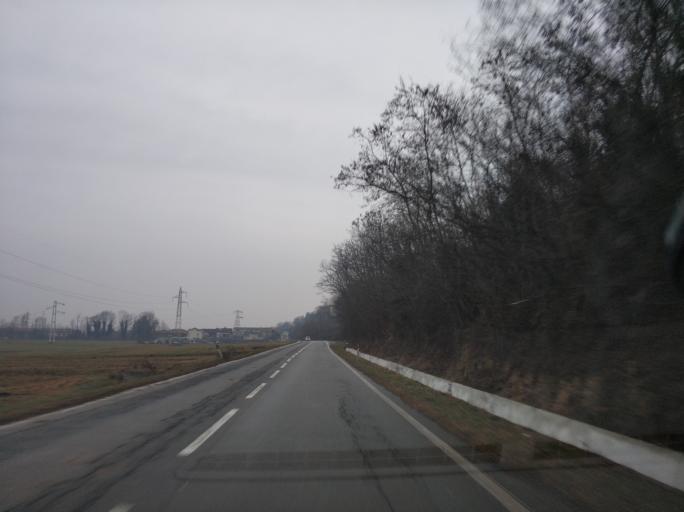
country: IT
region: Piedmont
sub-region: Provincia di Torino
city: San Francesco al Campo
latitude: 45.2259
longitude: 7.6521
